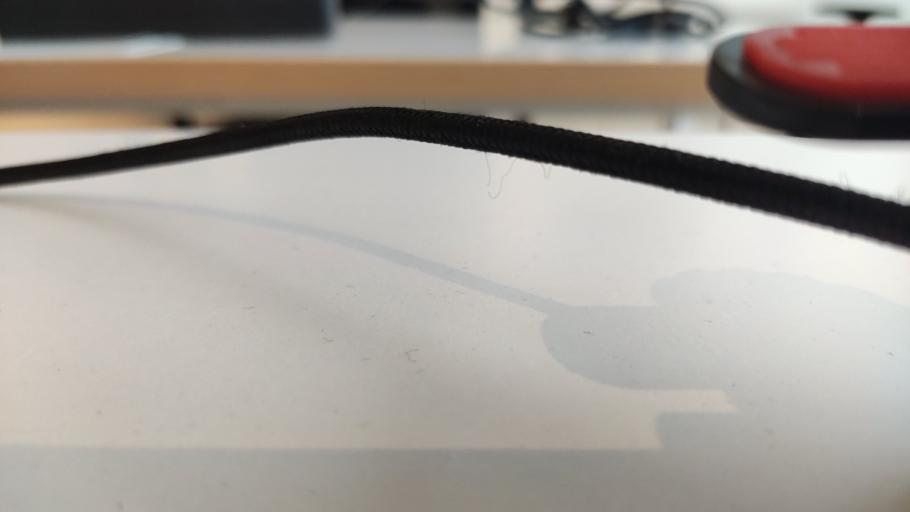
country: RU
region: Moskovskaya
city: Klin
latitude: 56.3525
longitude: 36.7486
